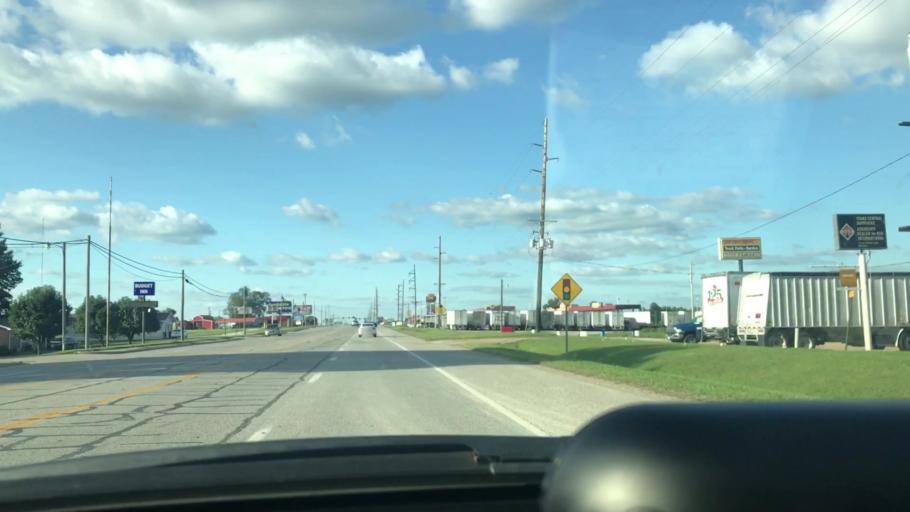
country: US
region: Missouri
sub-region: Pettis County
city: Sedalia
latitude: 38.6694
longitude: -93.2518
